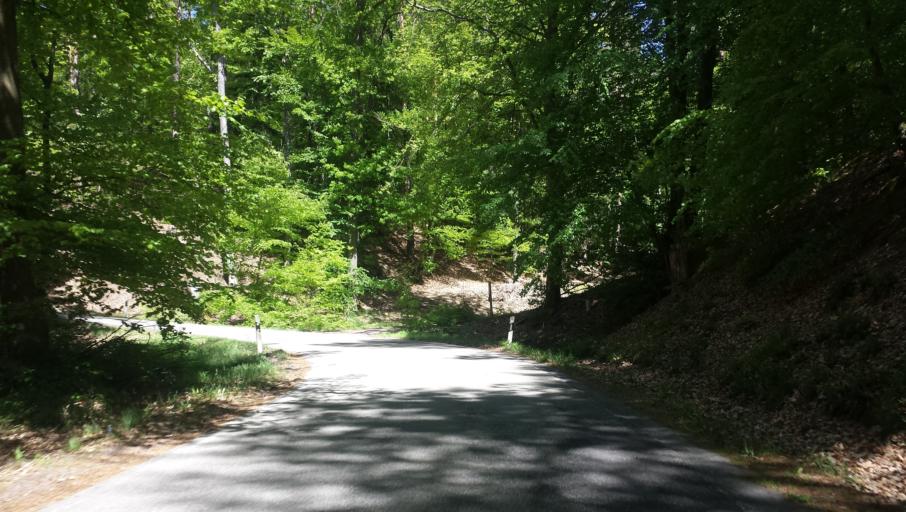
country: DE
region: Rheinland-Pfalz
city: Ramberg
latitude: 49.2958
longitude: 8.0160
